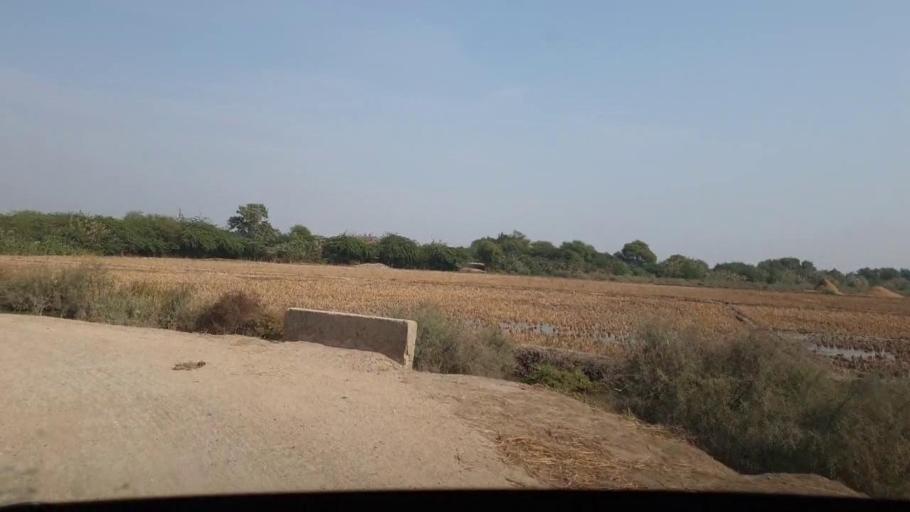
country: PK
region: Sindh
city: Chuhar Jamali
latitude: 24.2680
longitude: 67.9562
